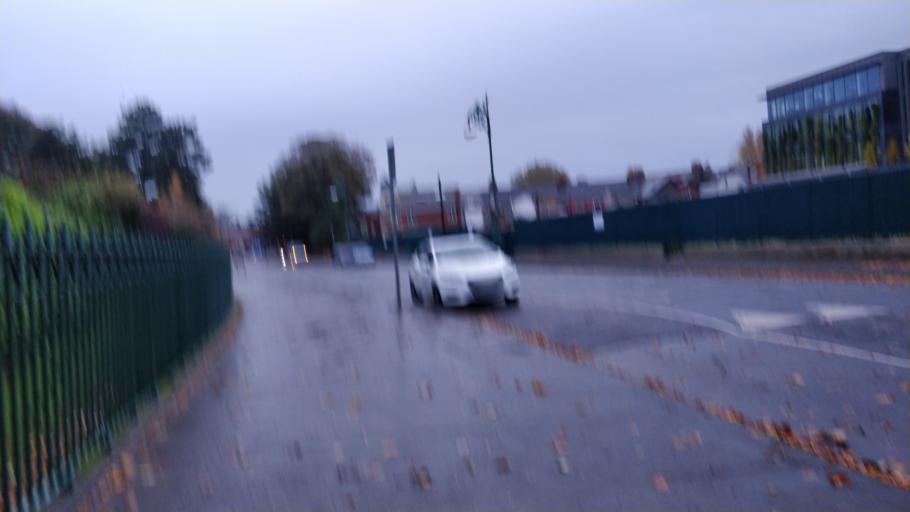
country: IE
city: Clonskeagh
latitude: 53.3284
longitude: -6.2341
